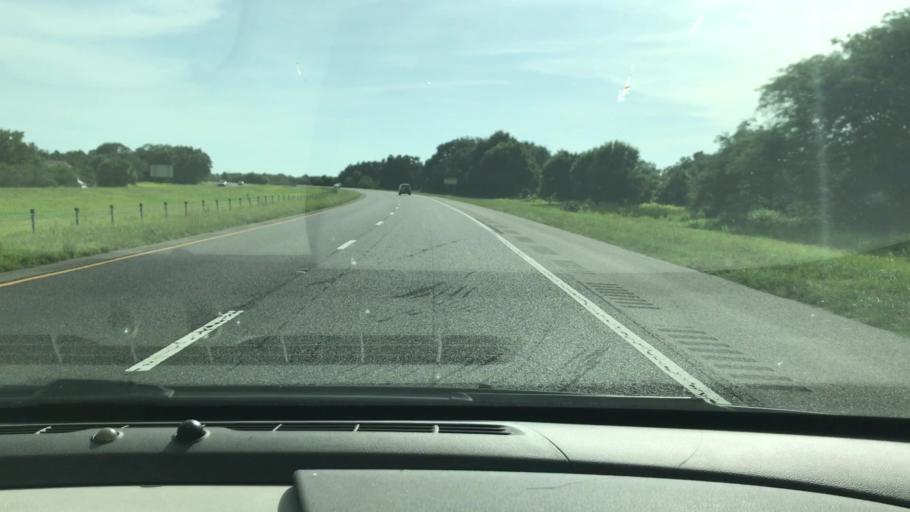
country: US
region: Florida
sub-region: Manatee County
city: Memphis
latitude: 27.5850
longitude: -82.5557
